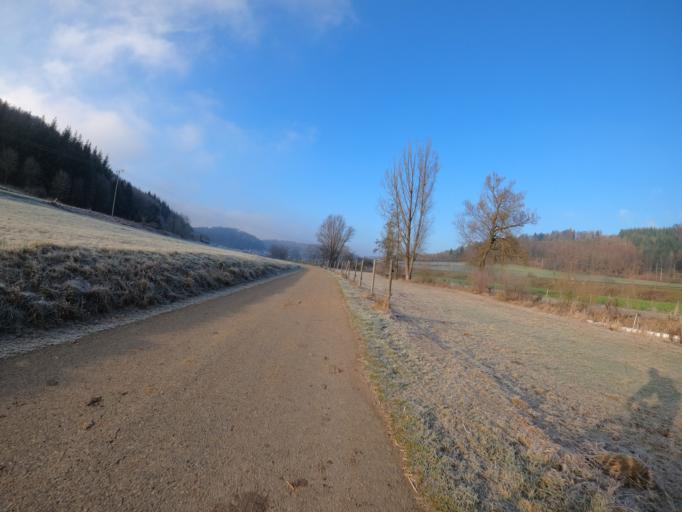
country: DE
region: Baden-Wuerttemberg
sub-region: Tuebingen Region
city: Lonsee
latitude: 48.5476
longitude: 9.9095
